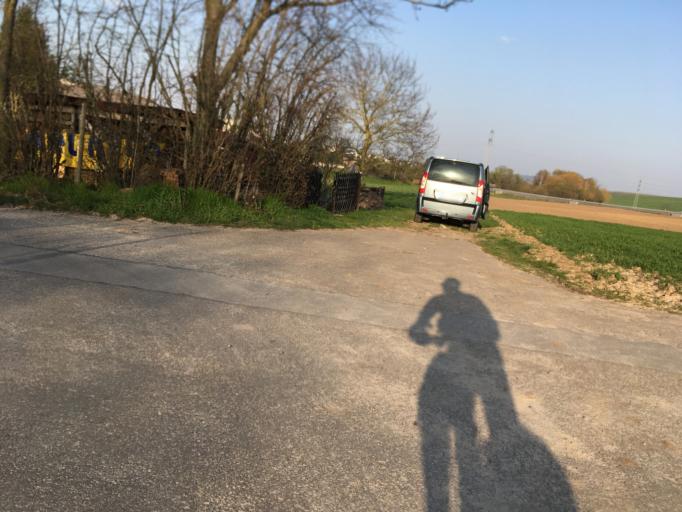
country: DE
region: Baden-Wuerttemberg
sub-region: Regierungsbezirk Stuttgart
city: Nordheim
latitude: 49.1012
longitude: 9.1095
